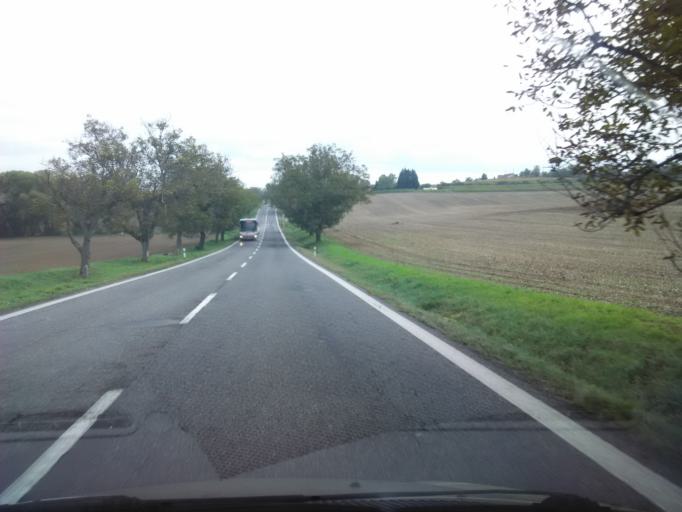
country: SK
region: Nitriansky
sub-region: Okres Nitra
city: Vrable
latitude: 48.2623
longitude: 18.2810
